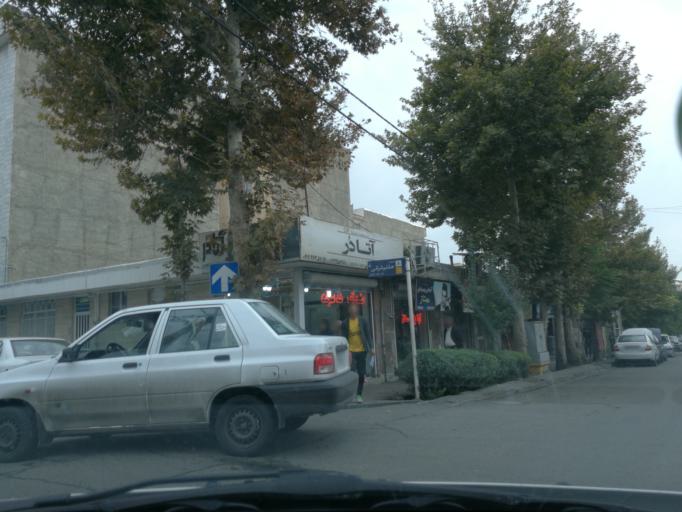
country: IR
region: Alborz
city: Karaj
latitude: 35.8552
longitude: 50.9528
